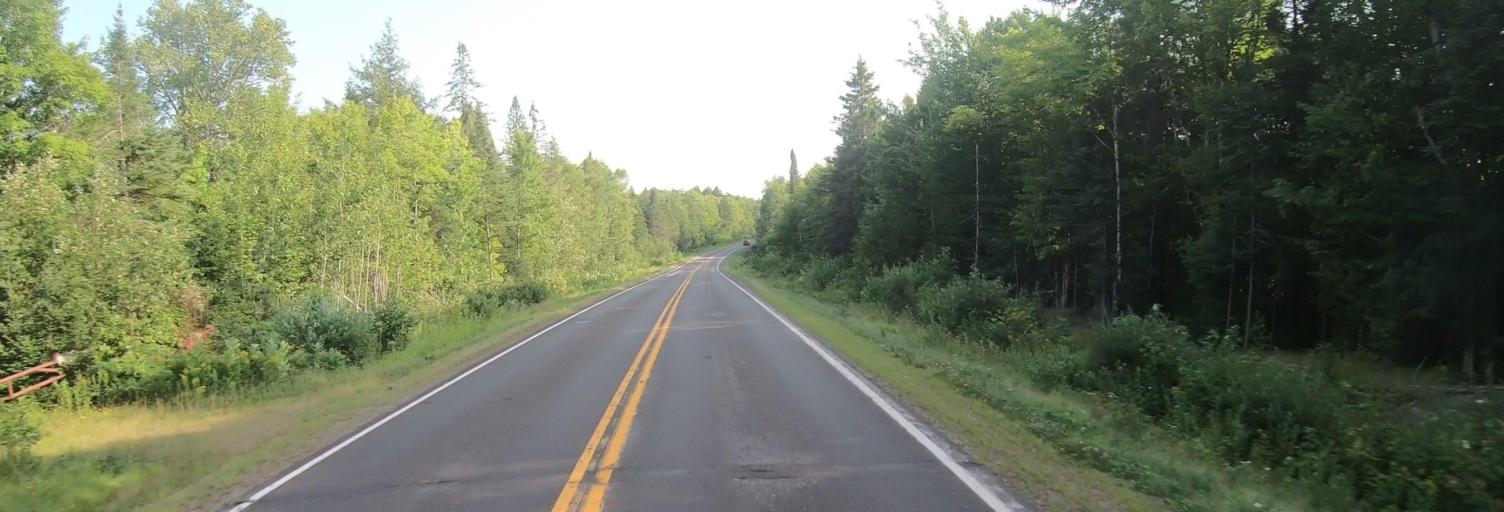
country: US
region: Wisconsin
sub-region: Ashland County
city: Ashland
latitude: 46.2483
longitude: -90.8313
